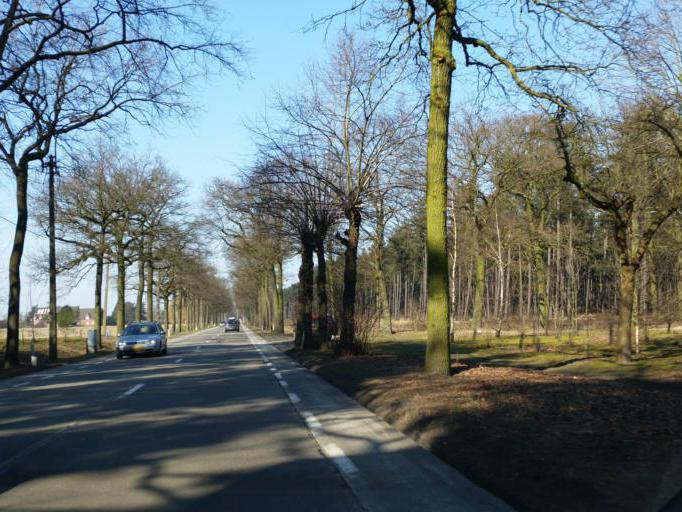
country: BE
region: Flanders
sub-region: Provincie Oost-Vlaanderen
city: Zelzate
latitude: 51.1830
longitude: 3.8373
